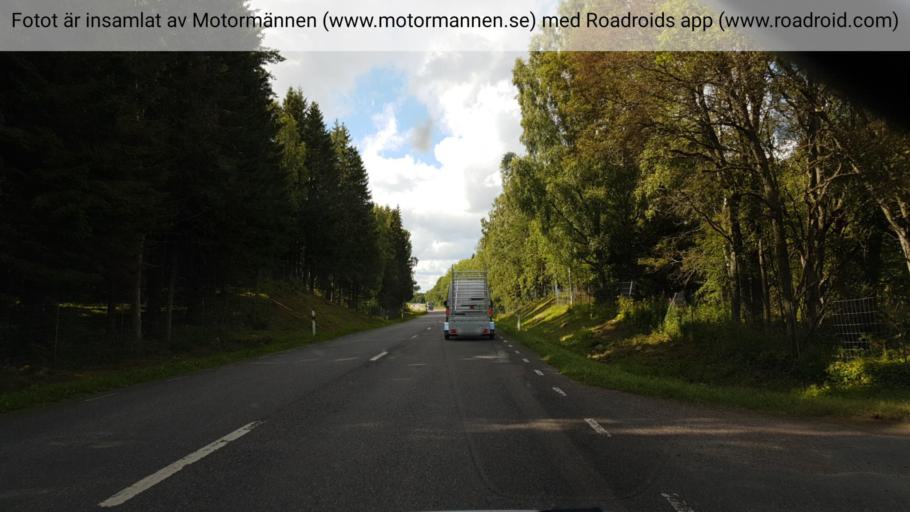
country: SE
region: Vaestra Goetaland
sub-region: Falkopings Kommun
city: Falkoeping
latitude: 58.0607
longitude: 13.5389
